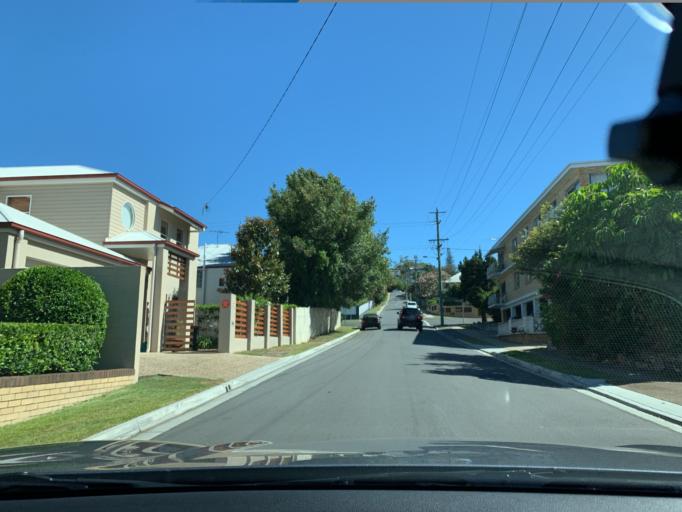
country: AU
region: Queensland
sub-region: Brisbane
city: Ascot
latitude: -27.4280
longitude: 153.0525
